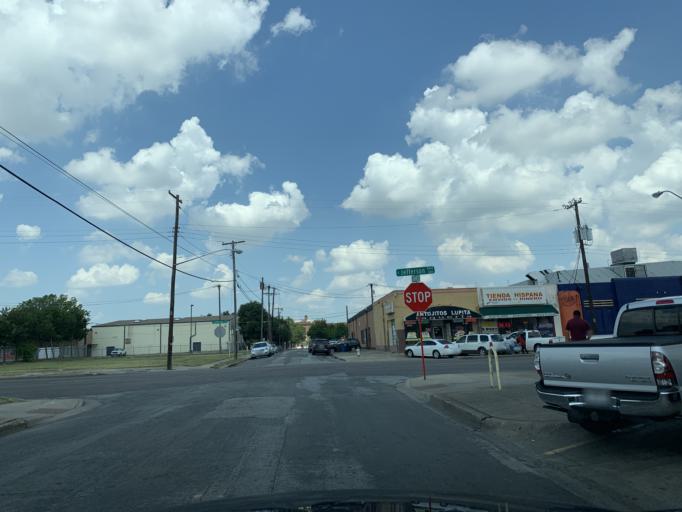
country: US
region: Texas
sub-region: Dallas County
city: Dallas
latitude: 32.7445
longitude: -96.8203
